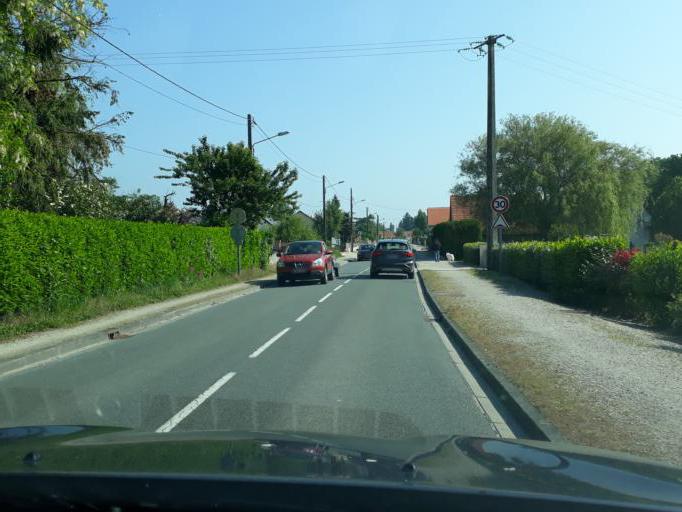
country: FR
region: Centre
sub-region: Departement du Loiret
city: Trainou
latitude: 47.9675
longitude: 2.0991
